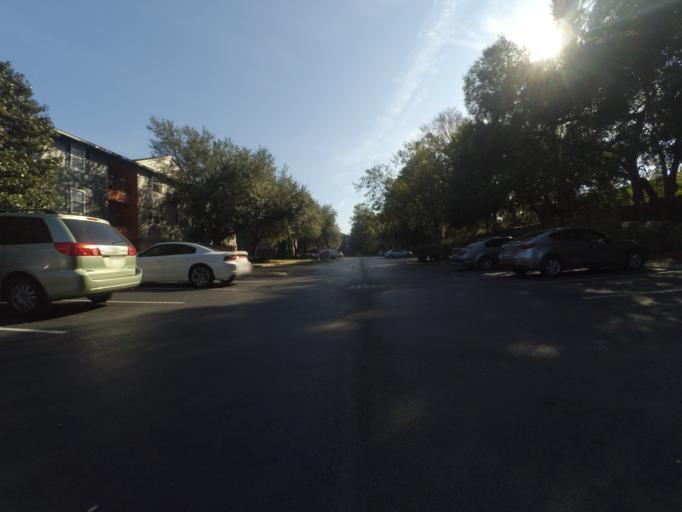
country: US
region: Florida
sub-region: Alachua County
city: Gainesville
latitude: 29.6165
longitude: -82.3648
